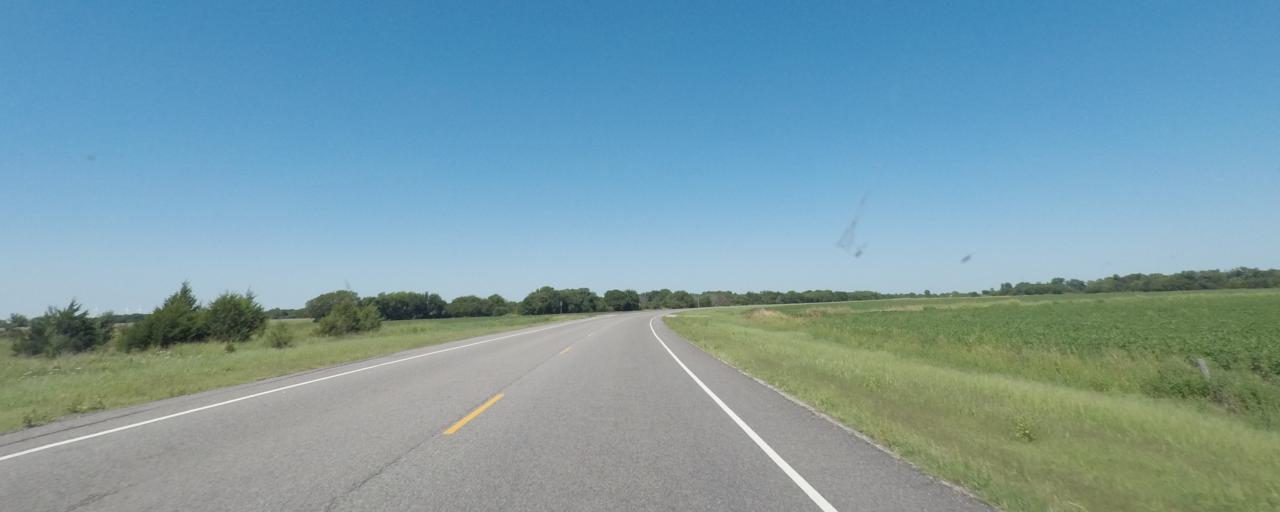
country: US
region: Oklahoma
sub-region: Kay County
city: Blackwell
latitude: 36.9421
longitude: -97.3532
